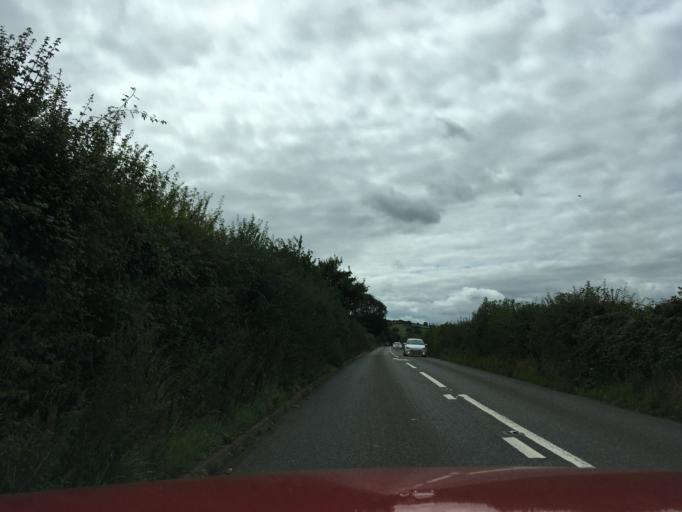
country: GB
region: England
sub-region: Devon
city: Bradninch
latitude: 50.8258
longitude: -3.3946
